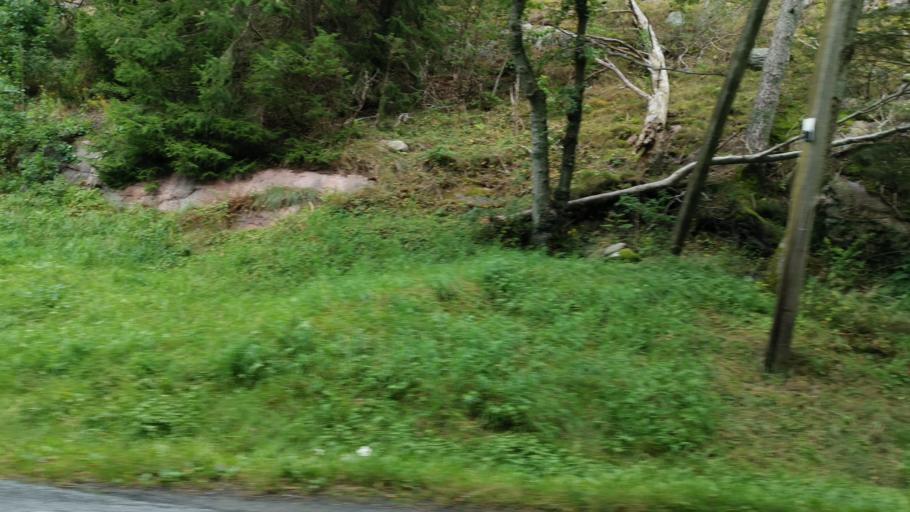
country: SE
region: Vaestra Goetaland
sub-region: Tjorns Kommun
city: Skaerhamn
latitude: 58.0417
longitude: 11.6435
